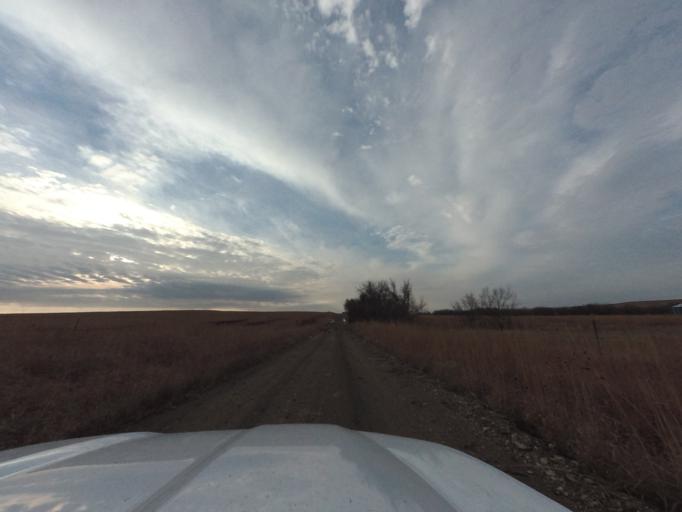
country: US
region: Kansas
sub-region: Chase County
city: Cottonwood Falls
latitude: 38.4545
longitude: -96.4471
